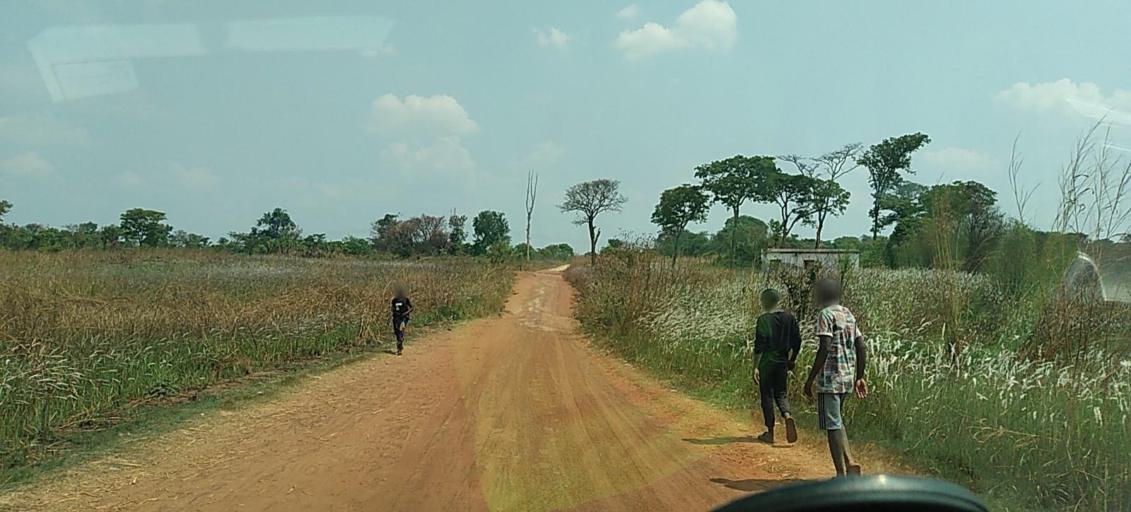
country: ZM
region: North-Western
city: Solwezi
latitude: -12.1122
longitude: 26.3671
